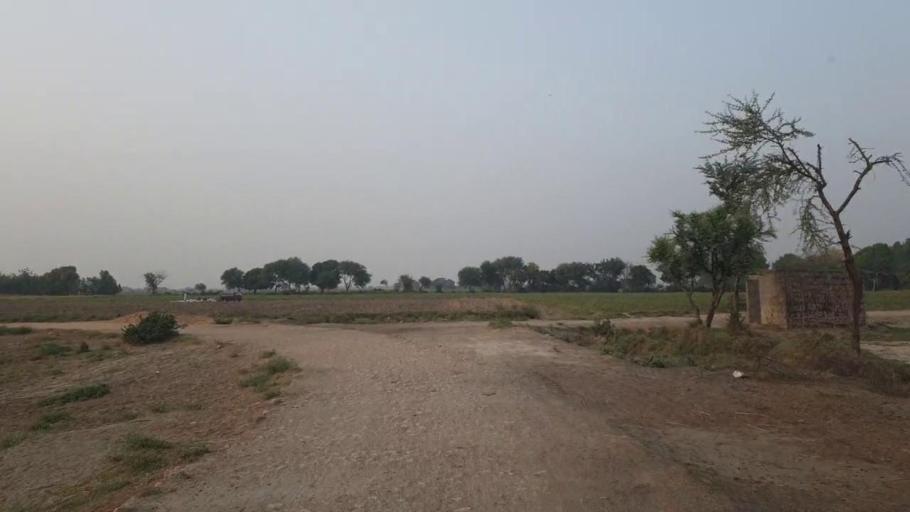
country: PK
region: Sindh
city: Mirpur Batoro
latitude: 24.6630
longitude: 68.3845
